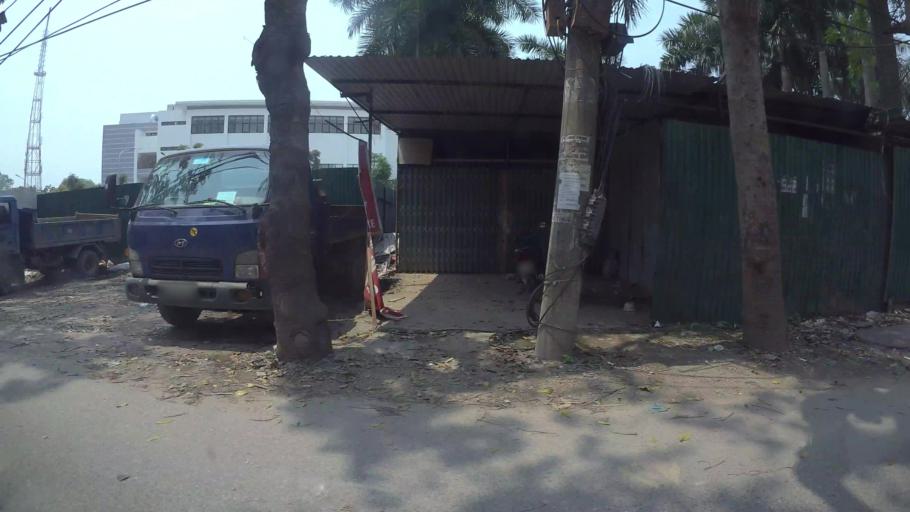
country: VN
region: Ha Noi
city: Thanh Xuan
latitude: 20.9978
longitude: 105.7884
